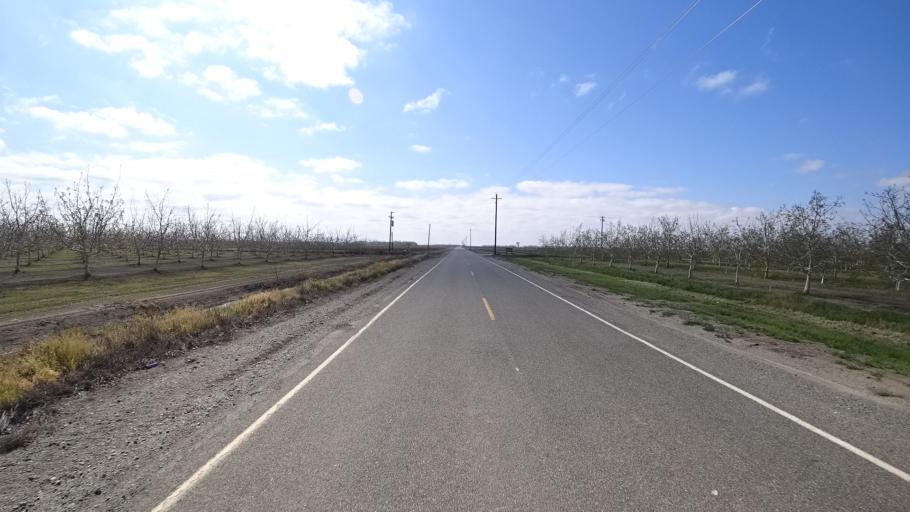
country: US
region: California
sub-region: Butte County
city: Biggs
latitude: 39.4428
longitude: -121.9301
